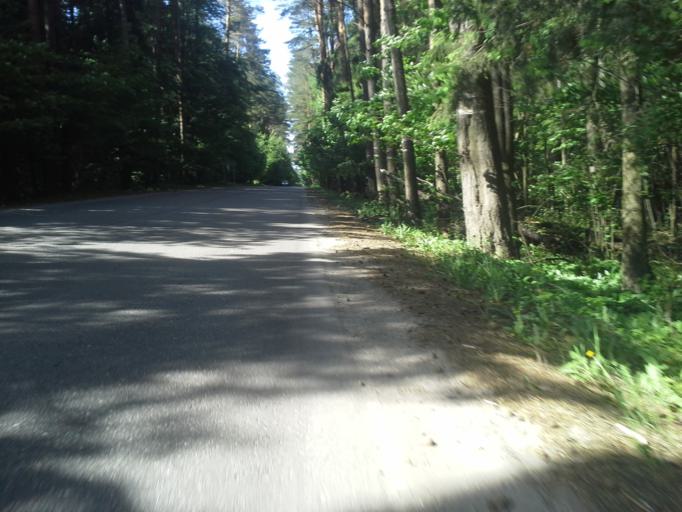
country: RU
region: Moskovskaya
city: Dubrovitsy
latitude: 55.4324
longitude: 37.3990
